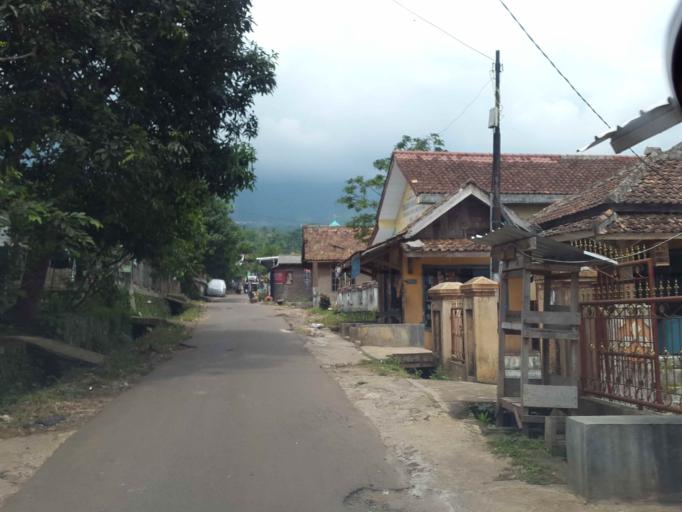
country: ID
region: Banten
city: Cilaja
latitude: -6.3137
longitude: 106.0848
